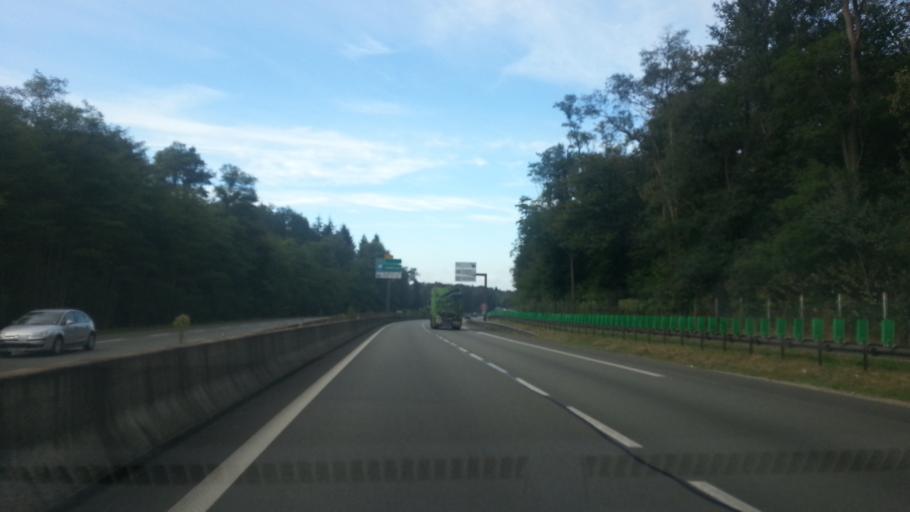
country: FR
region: Picardie
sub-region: Departement de l'Oise
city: Avilly-Saint-Leonard
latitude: 49.2273
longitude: 2.5420
